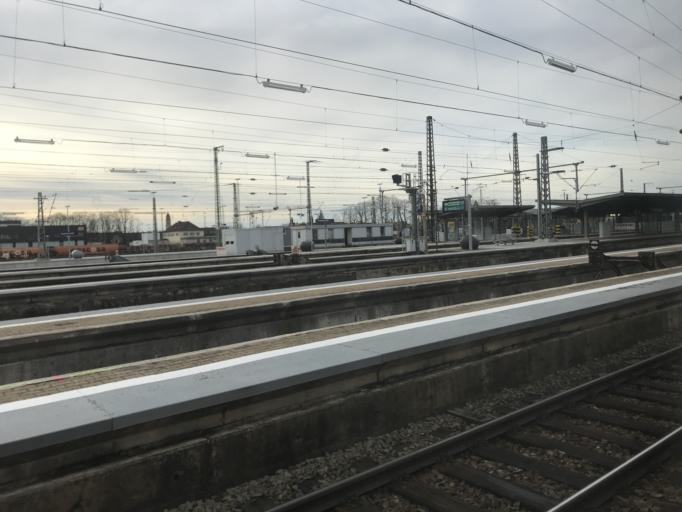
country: DE
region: Bavaria
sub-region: Swabia
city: Augsburg
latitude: 48.3641
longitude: 10.8871
